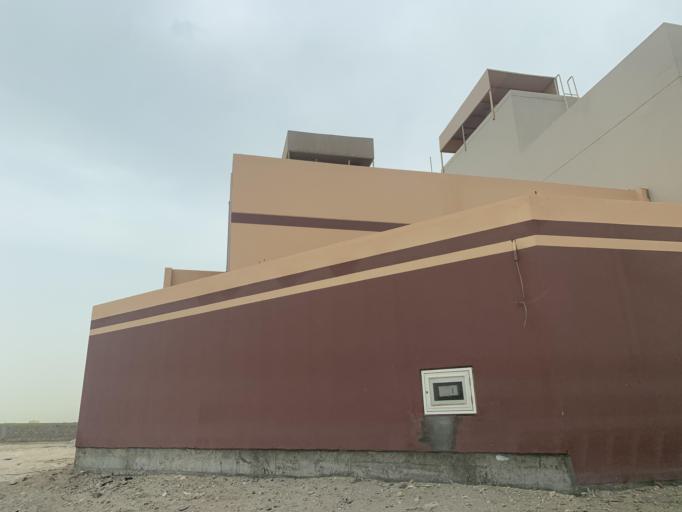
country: BH
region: Northern
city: Madinat `Isa
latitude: 26.1797
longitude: 50.5159
